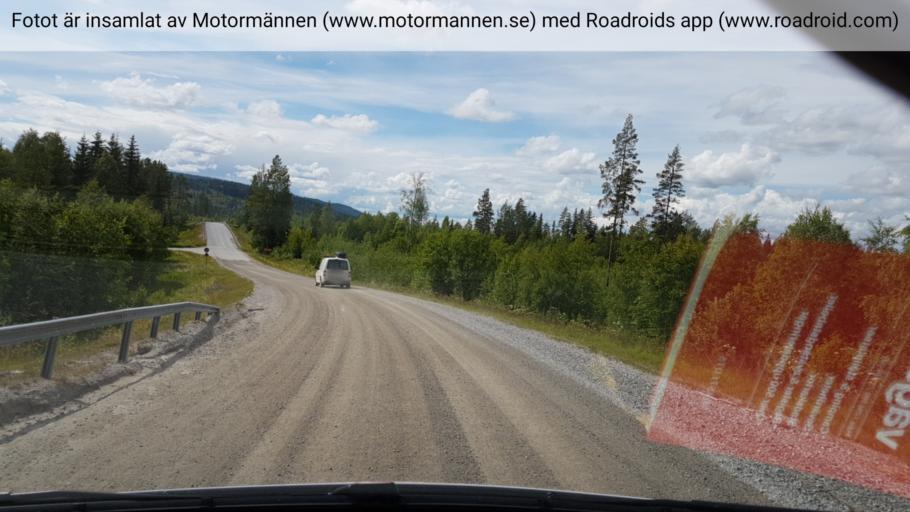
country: SE
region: Vaesternorrland
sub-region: Solleftea Kommun
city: Solleftea
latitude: 63.3152
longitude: 17.2173
